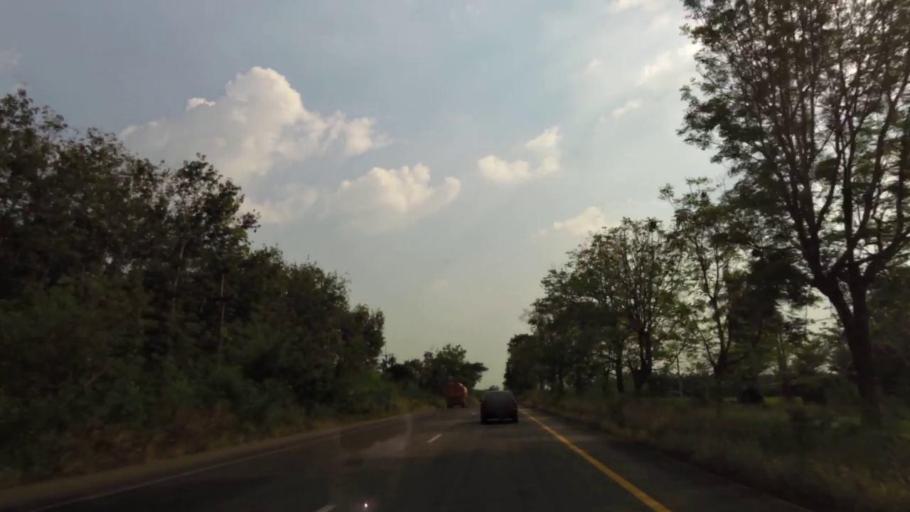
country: TH
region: Rayong
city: Wang Chan
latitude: 13.0015
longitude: 101.4829
